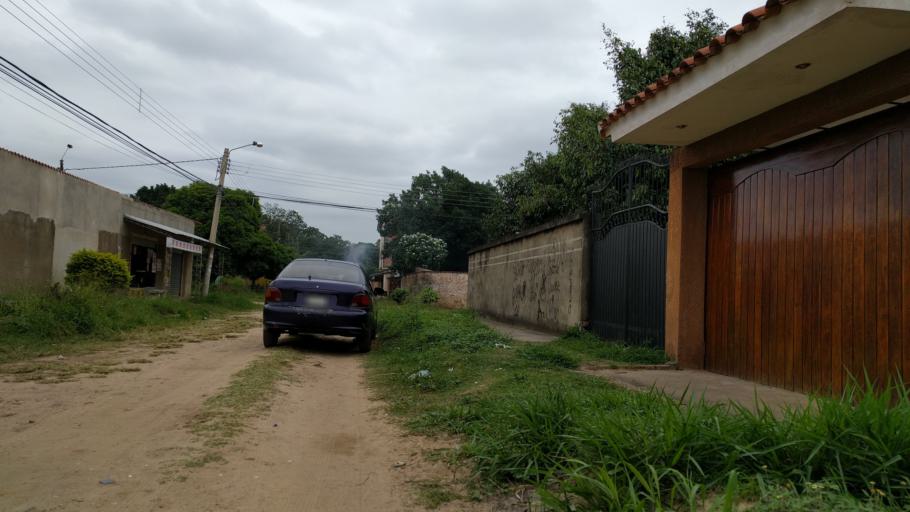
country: BO
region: Santa Cruz
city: Santa Cruz de la Sierra
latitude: -17.8068
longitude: -63.2179
